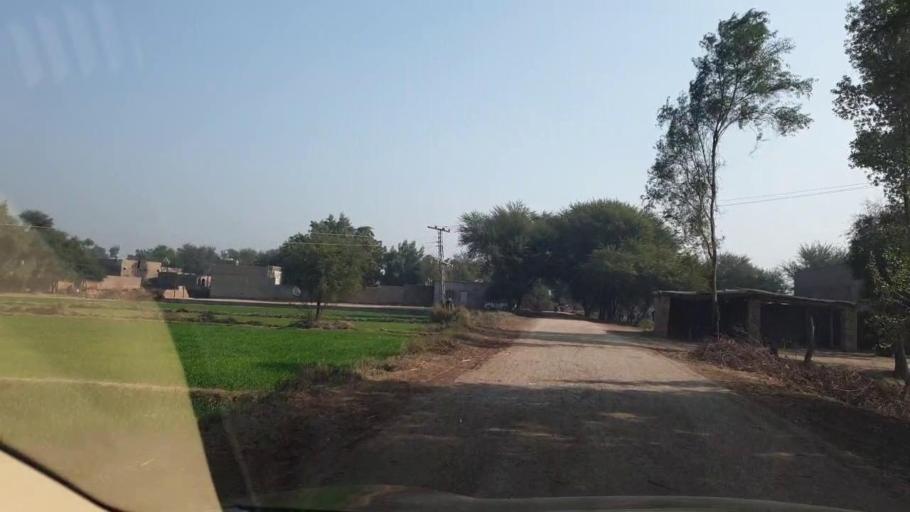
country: PK
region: Sindh
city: Ubauro
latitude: 28.1140
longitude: 69.7277
